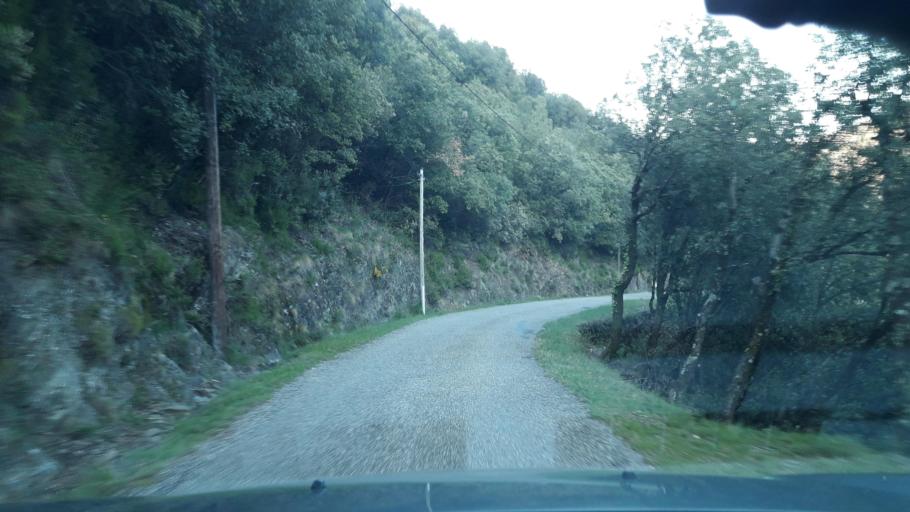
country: FR
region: Languedoc-Roussillon
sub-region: Departement du Gard
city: Valleraugue
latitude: 44.1075
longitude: 3.6665
